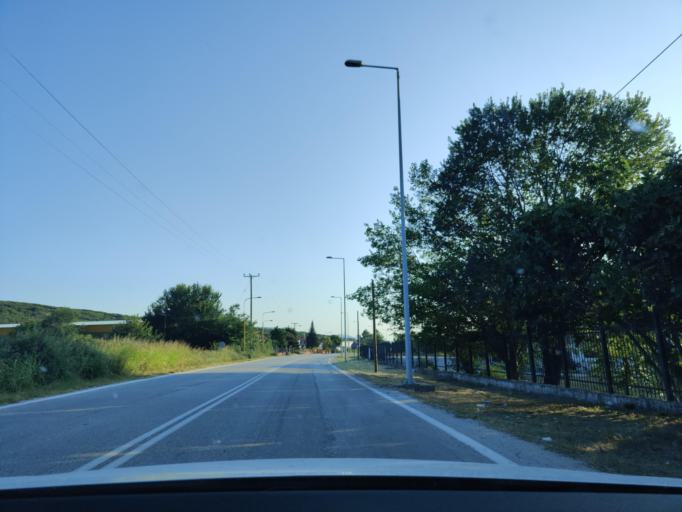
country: GR
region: East Macedonia and Thrace
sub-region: Nomos Kavalas
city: Amygdaleonas
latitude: 40.9775
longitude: 24.3642
